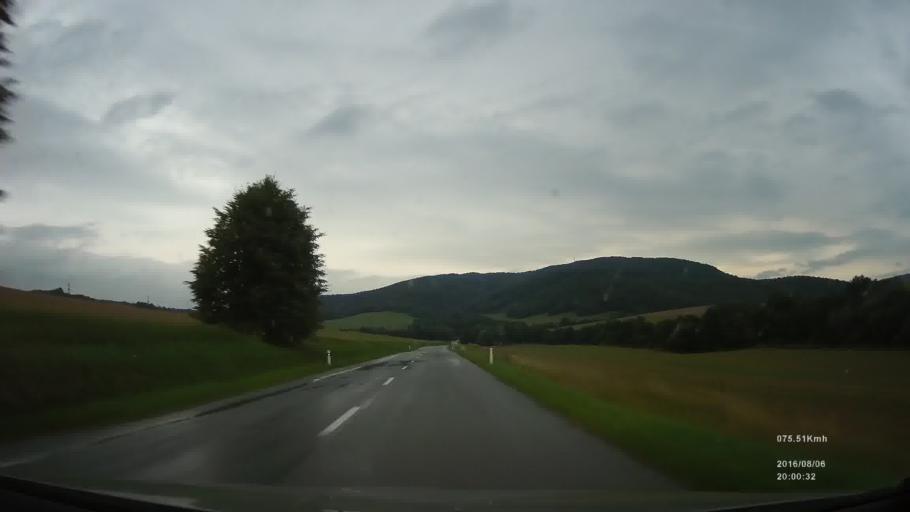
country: SK
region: Presovsky
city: Svidnik
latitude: 49.2515
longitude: 21.5819
